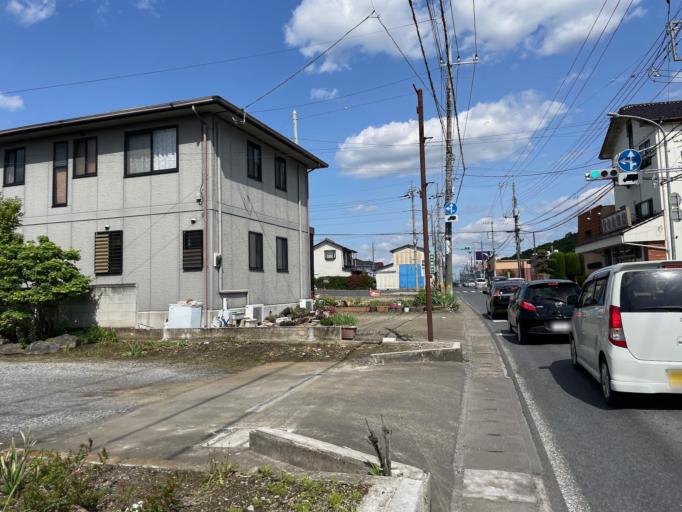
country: JP
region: Tochigi
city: Fujioka
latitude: 36.3195
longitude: 139.6597
